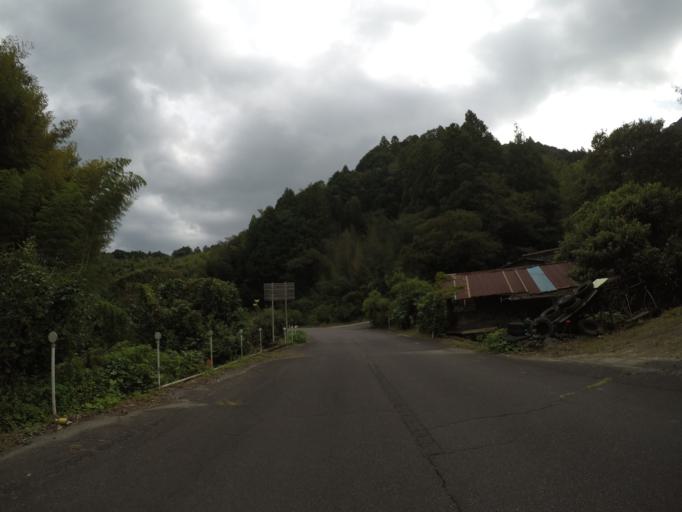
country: JP
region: Shizuoka
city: Fujieda
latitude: 34.9193
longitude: 138.2282
